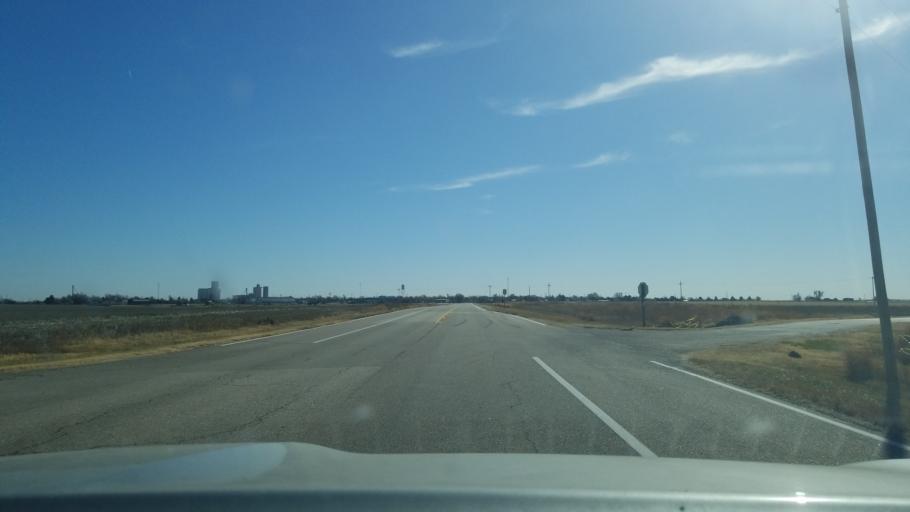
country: US
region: Kansas
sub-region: Kiowa County
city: Greensburg
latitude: 37.5591
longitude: -99.6486
